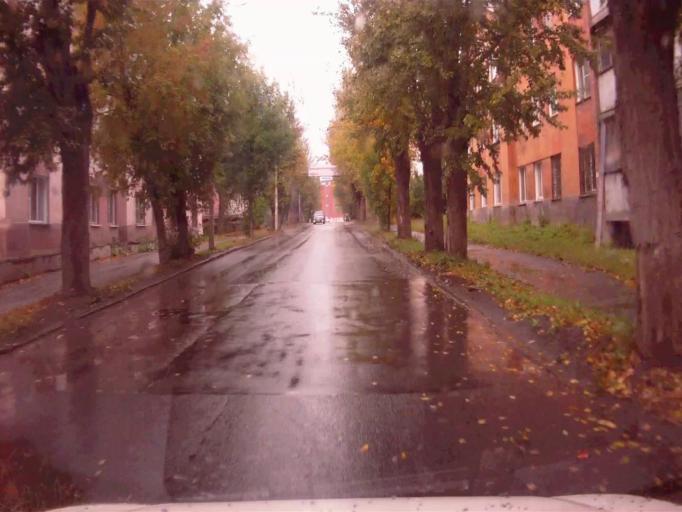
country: RU
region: Chelyabinsk
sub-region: Gorod Chelyabinsk
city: Chelyabinsk
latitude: 55.1969
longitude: 61.4083
